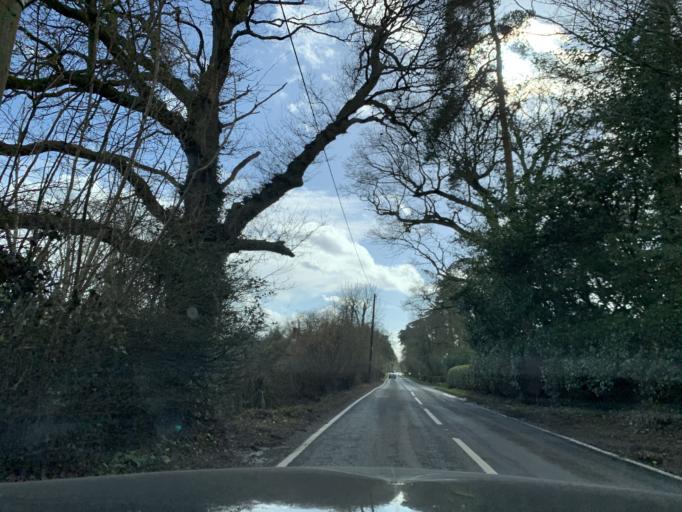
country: GB
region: England
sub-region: West Sussex
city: Crawley Down
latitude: 51.0836
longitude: -0.0773
